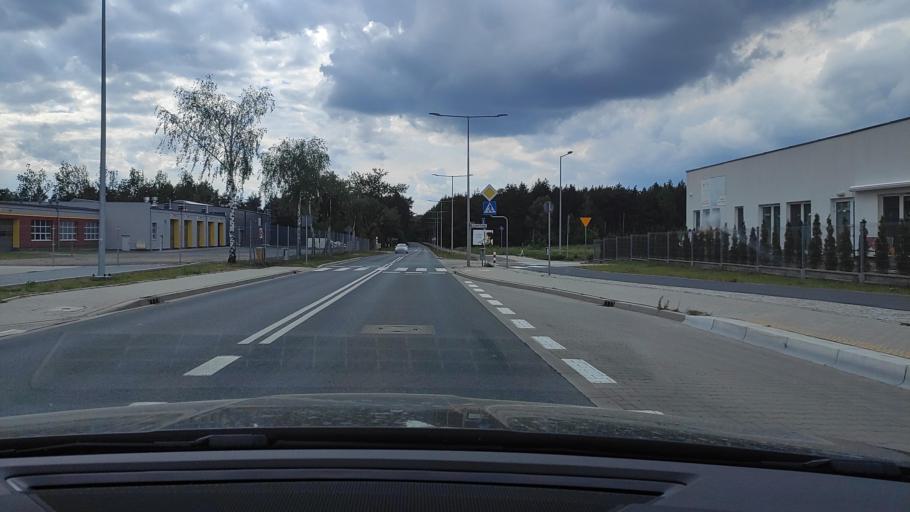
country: PL
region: Greater Poland Voivodeship
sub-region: Powiat poznanski
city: Swarzedz
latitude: 52.3837
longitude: 17.0600
